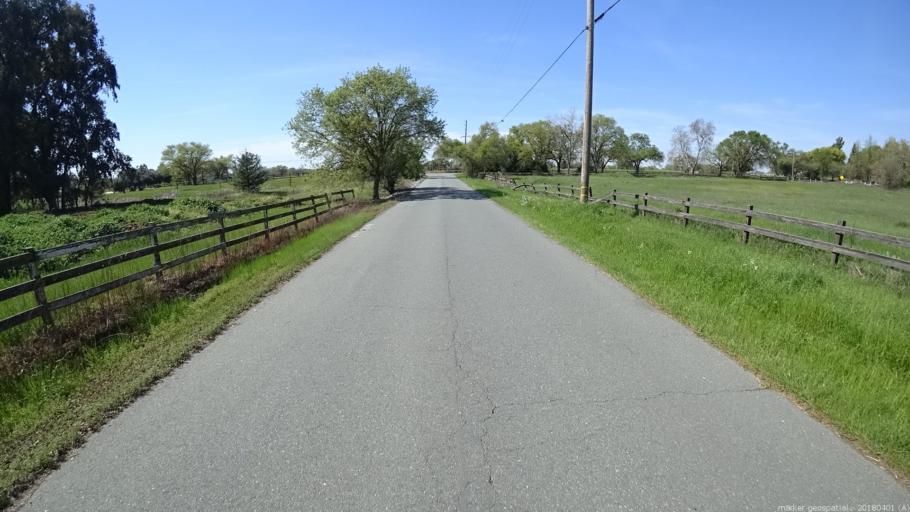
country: US
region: California
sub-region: Sacramento County
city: Wilton
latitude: 38.4147
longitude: -121.2545
